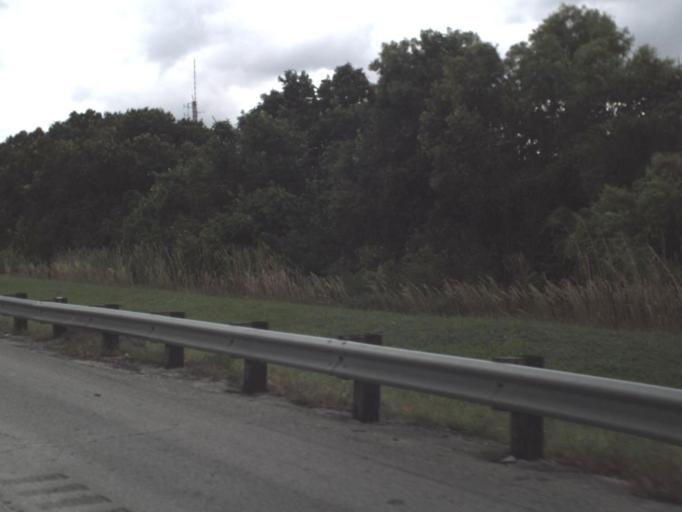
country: US
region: Florida
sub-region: Palm Beach County
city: Palm Beach Gardens
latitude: 26.8113
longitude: -80.1312
